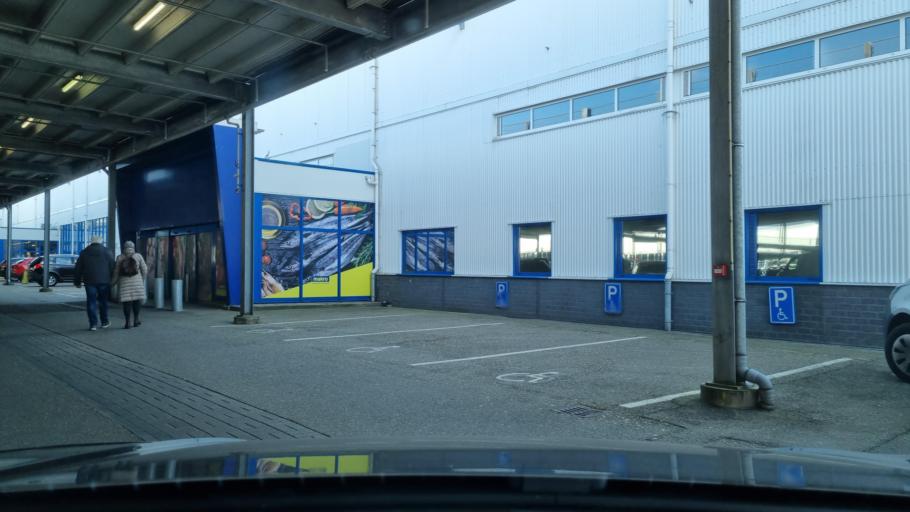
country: NL
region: Gelderland
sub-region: Gemeente Nijmegen
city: Lindenholt
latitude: 51.8416
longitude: 5.8198
